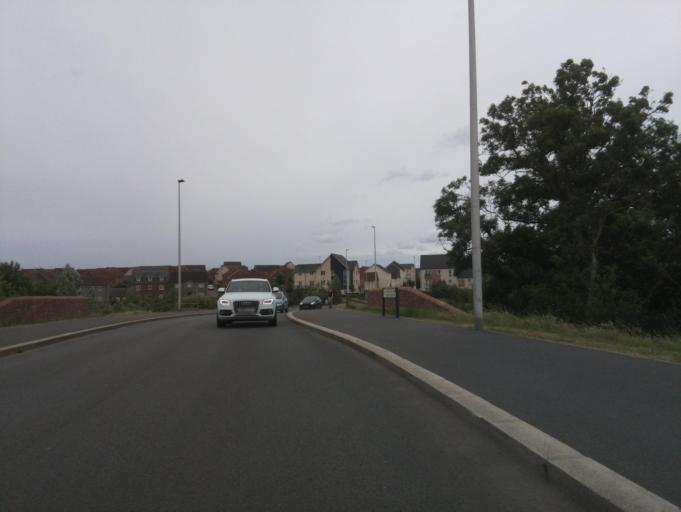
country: GB
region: England
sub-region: Devon
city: Bradninch
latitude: 50.7504
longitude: -3.4081
